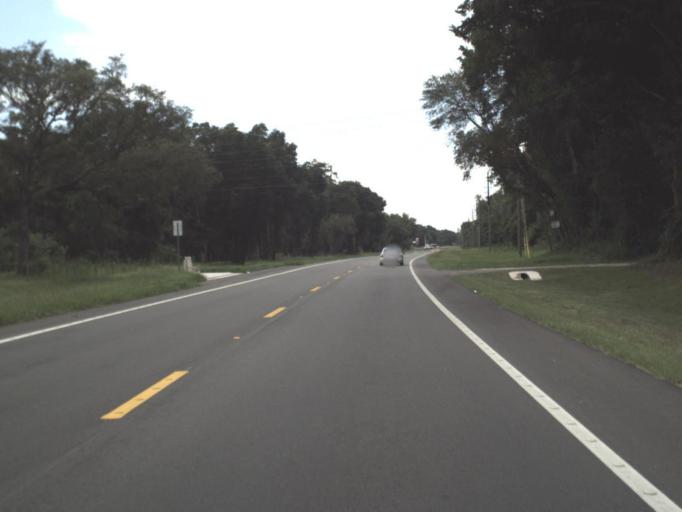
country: US
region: Florida
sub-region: Pasco County
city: Lacoochee
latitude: 28.4571
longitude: -82.1886
